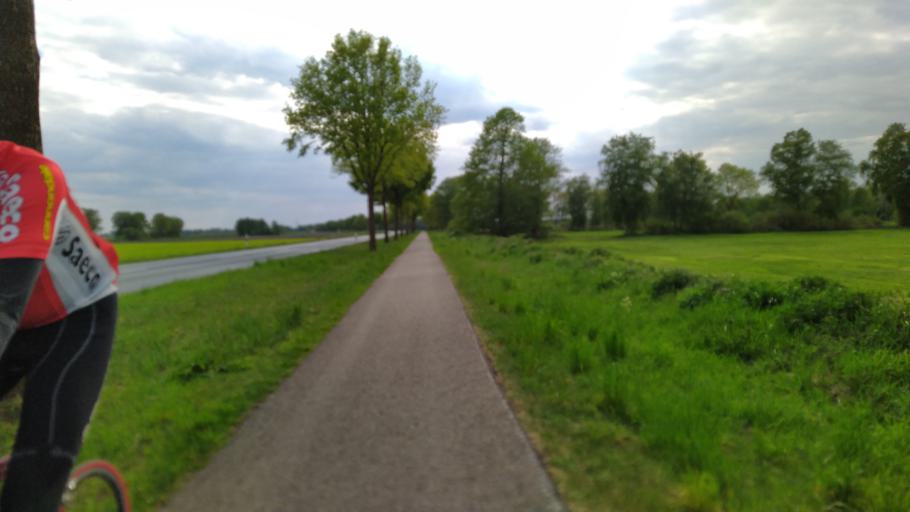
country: DE
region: Lower Saxony
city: Tarmstedt
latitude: 53.2114
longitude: 9.0455
